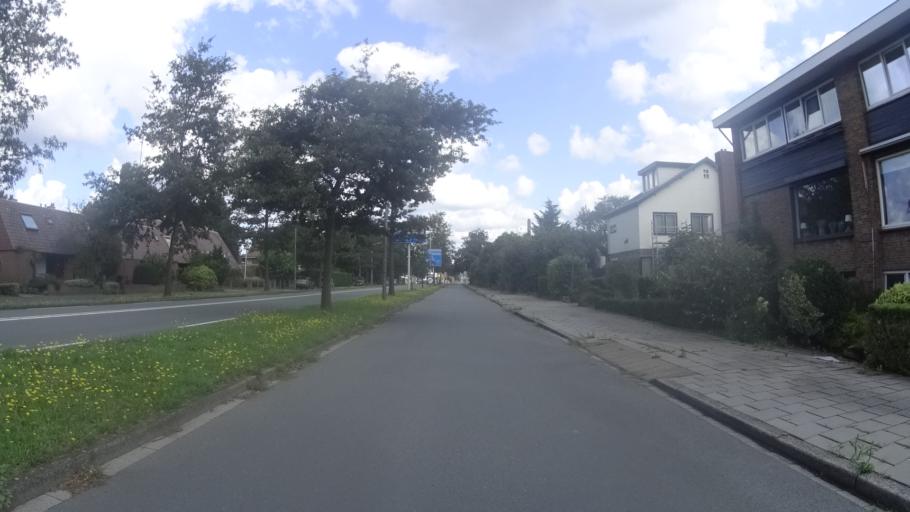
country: NL
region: North Holland
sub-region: Gemeente Velsen
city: Velsen-Zuid
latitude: 52.4595
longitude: 4.6334
